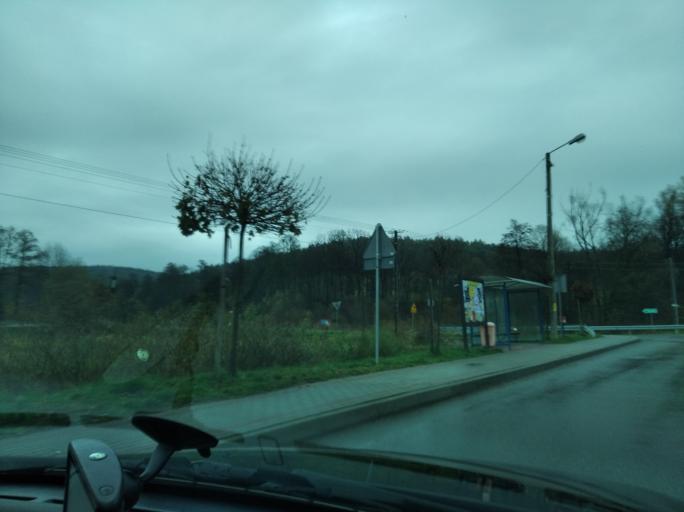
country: PL
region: Subcarpathian Voivodeship
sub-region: Powiat rzeszowski
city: Lecka
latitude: 49.8985
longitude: 22.0080
